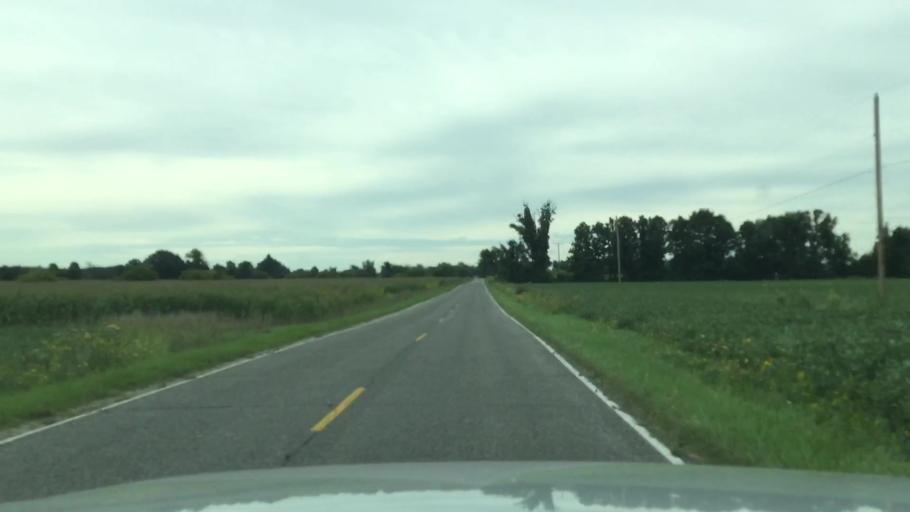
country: US
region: Michigan
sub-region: Genesee County
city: Flushing
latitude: 43.0680
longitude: -83.9876
